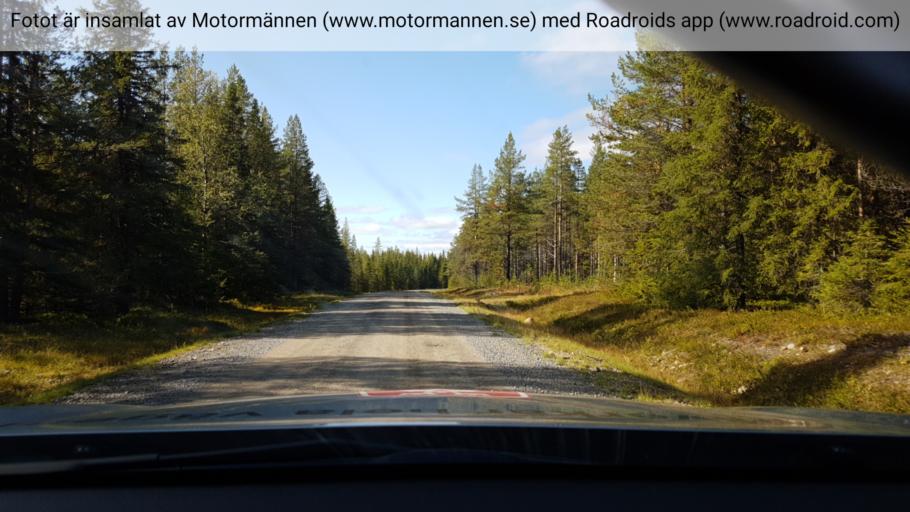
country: SE
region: Vaesterbotten
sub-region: Mala Kommun
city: Mala
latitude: 65.2111
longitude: 19.0731
